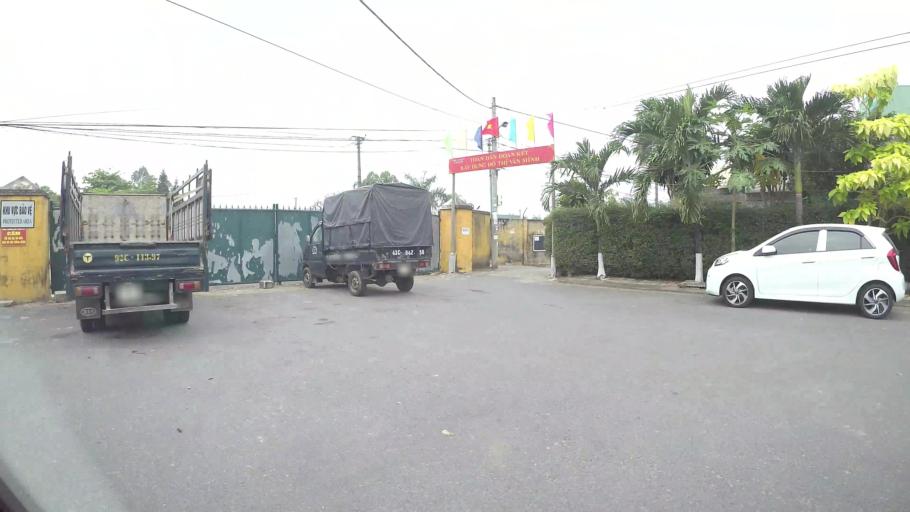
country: VN
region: Da Nang
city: Cam Le
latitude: 16.0421
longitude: 108.2060
